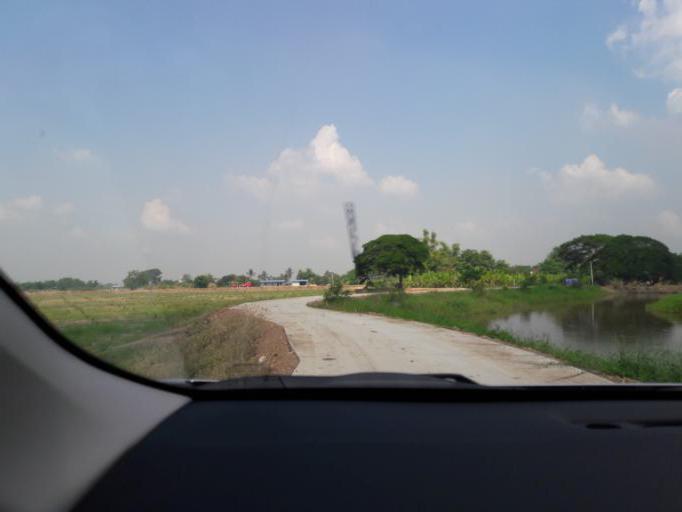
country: TH
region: Ang Thong
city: Ang Thong
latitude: 14.5637
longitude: 100.4145
